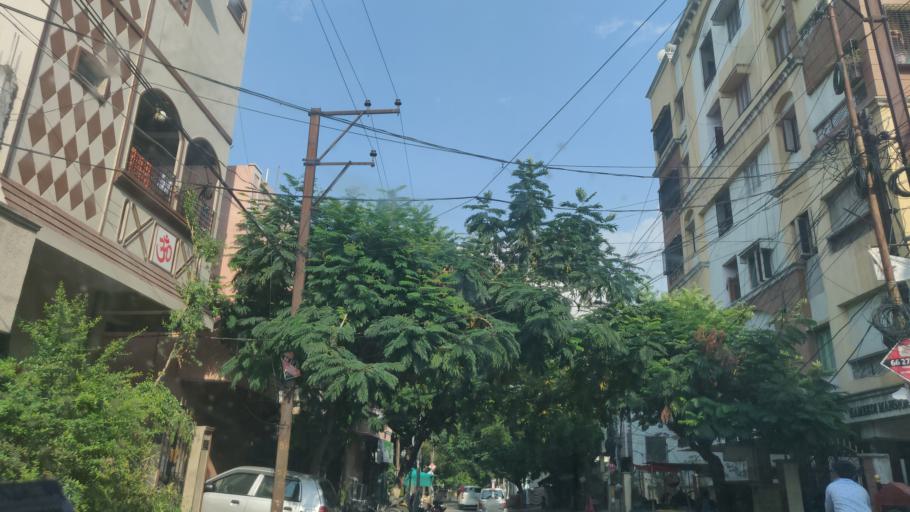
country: IN
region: Telangana
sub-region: Rangareddi
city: Gaddi Annaram
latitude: 17.3760
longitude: 78.5173
